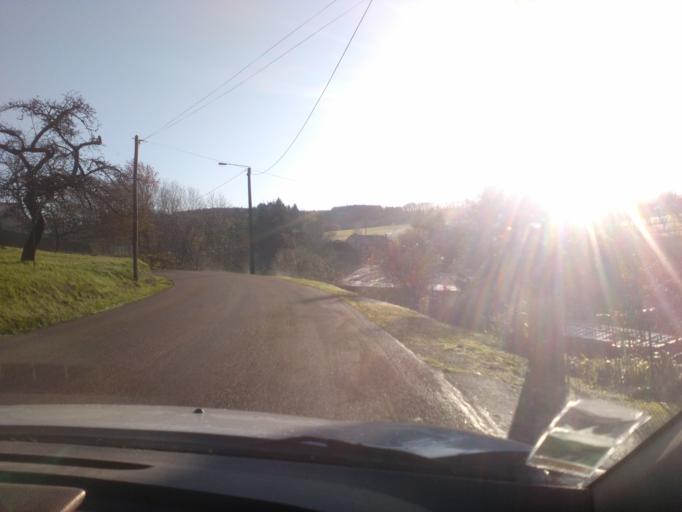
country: FR
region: Lorraine
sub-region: Departement des Vosges
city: Xertigny
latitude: 48.0473
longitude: 6.3874
